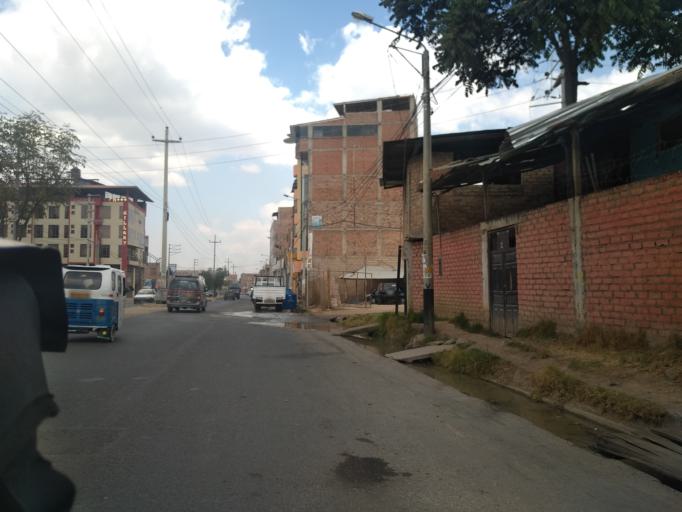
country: PE
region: Cajamarca
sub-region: Provincia de Cajamarca
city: Cajamarca
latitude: -7.1734
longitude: -78.4935
